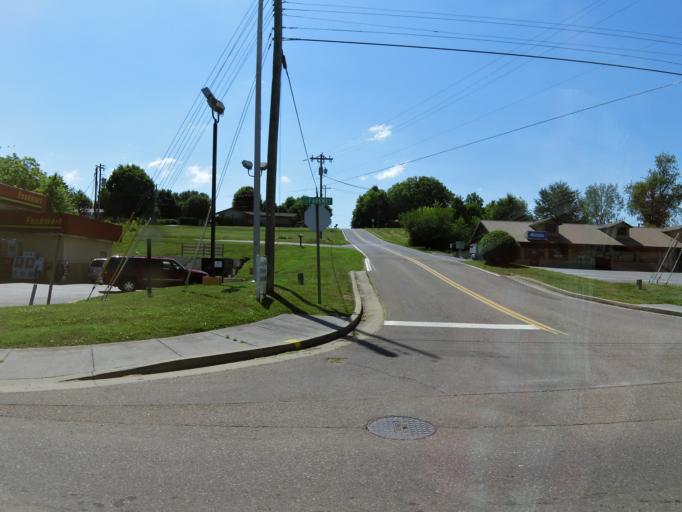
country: US
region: Tennessee
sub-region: Sevier County
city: Sevierville
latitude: 35.8415
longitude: -83.5710
